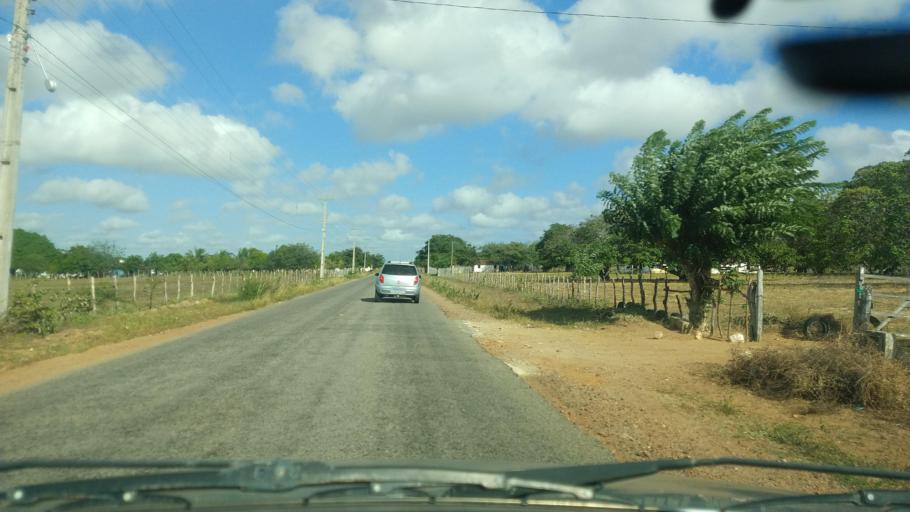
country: BR
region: Rio Grande do Norte
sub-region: Sao Paulo Do Potengi
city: Sao Paulo do Potengi
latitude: -5.9158
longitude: -35.7158
